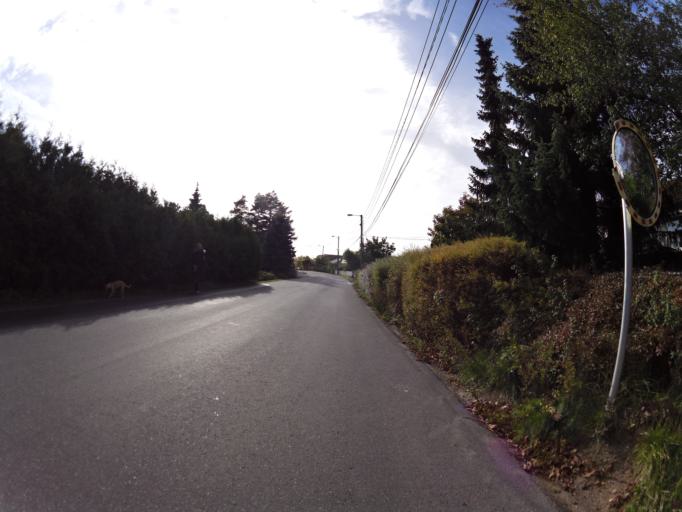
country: NO
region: Ostfold
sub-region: Fredrikstad
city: Fredrikstad
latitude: 59.2346
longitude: 10.9661
